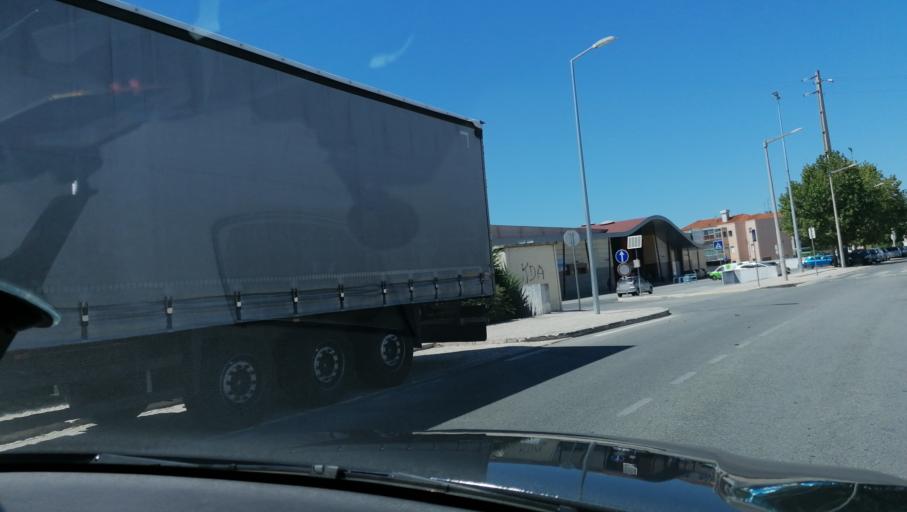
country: PT
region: Leiria
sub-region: Leiria
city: Leiria
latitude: 39.7602
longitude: -8.8214
